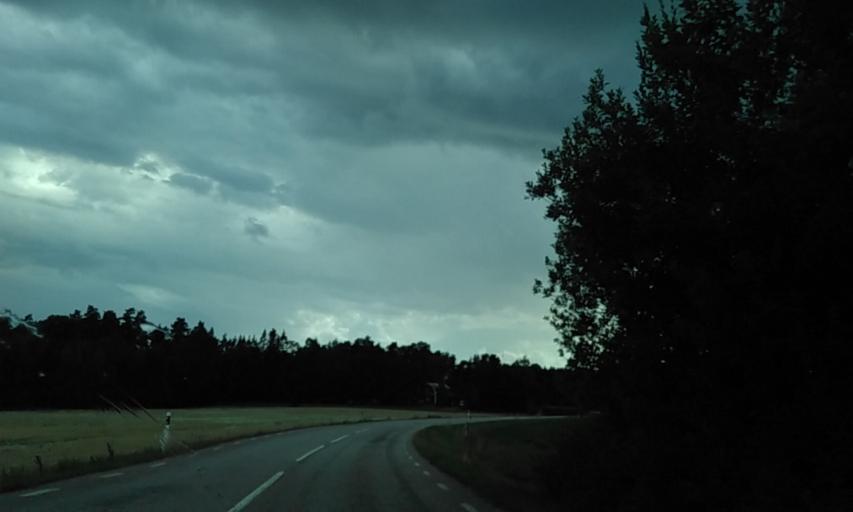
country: SE
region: Vaestra Goetaland
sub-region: Grastorps Kommun
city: Graestorp
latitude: 58.4794
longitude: 12.8590
